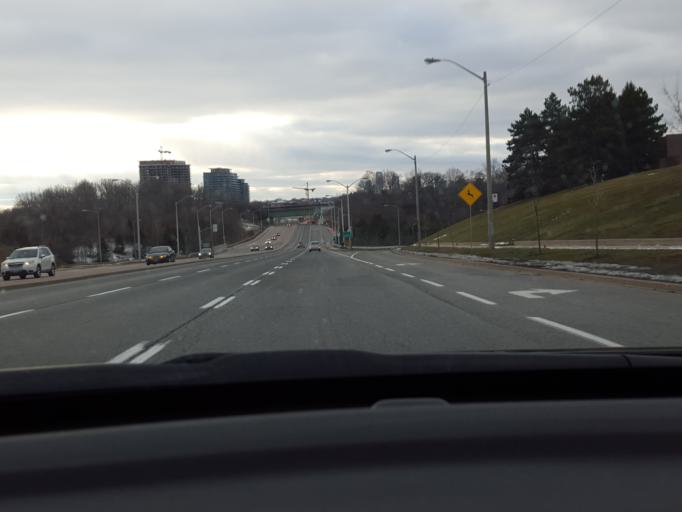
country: CA
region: Ontario
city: Willowdale
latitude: 43.7196
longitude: -79.3421
